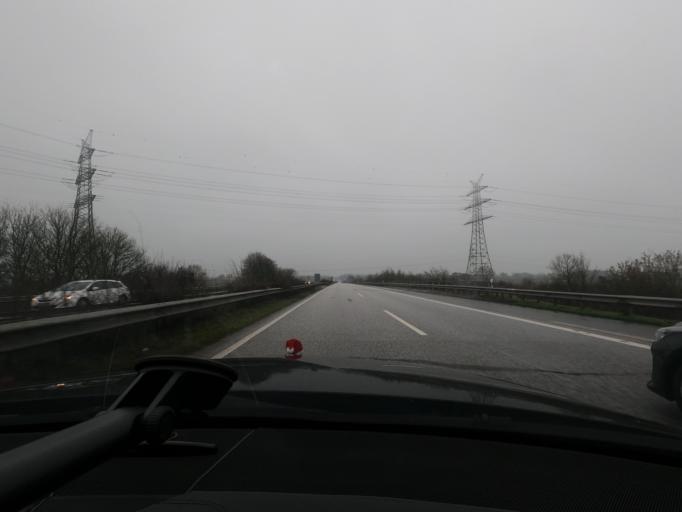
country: DE
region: Schleswig-Holstein
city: Schulldorf
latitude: 54.2978
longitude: 9.7599
